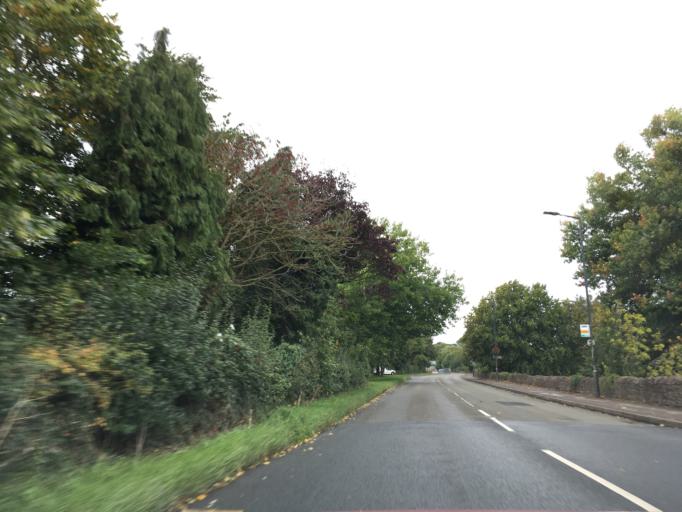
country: GB
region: England
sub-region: Herefordshire
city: Ross on Wye
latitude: 51.9130
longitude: -2.5924
